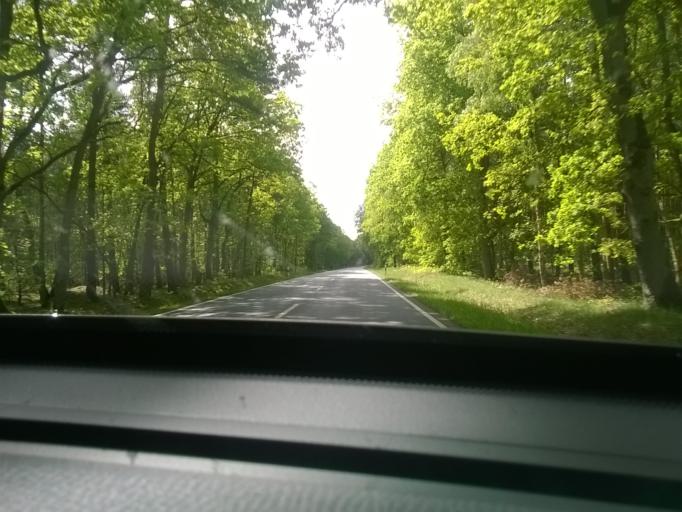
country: DE
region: Brandenburg
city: Wittstock
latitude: 53.1093
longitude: 12.4851
